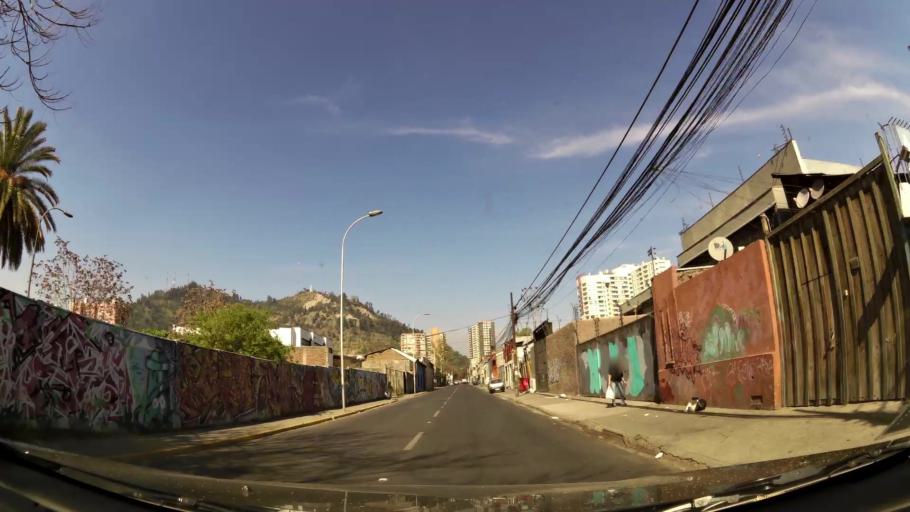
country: CL
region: Santiago Metropolitan
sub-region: Provincia de Santiago
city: Santiago
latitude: -33.4243
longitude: -70.6482
